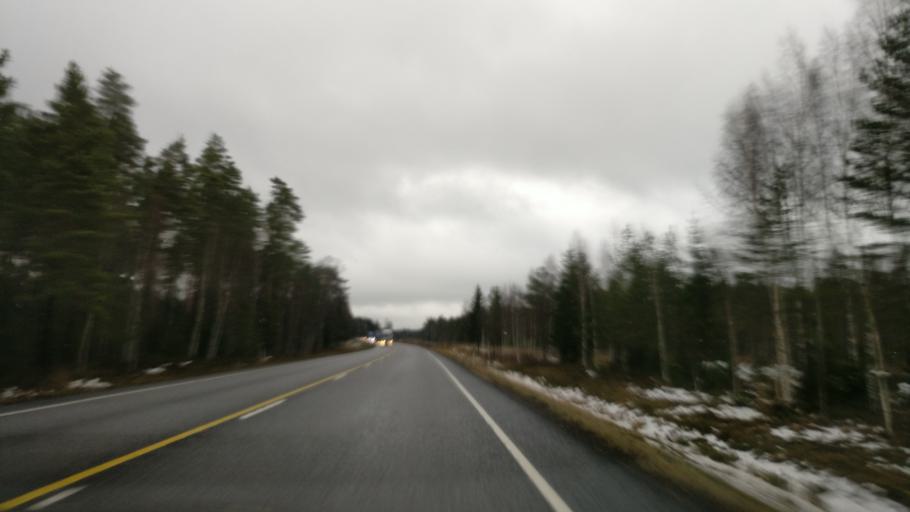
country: FI
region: Uusimaa
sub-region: Raaseporin
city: Ekenaes
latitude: 59.9383
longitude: 23.3361
